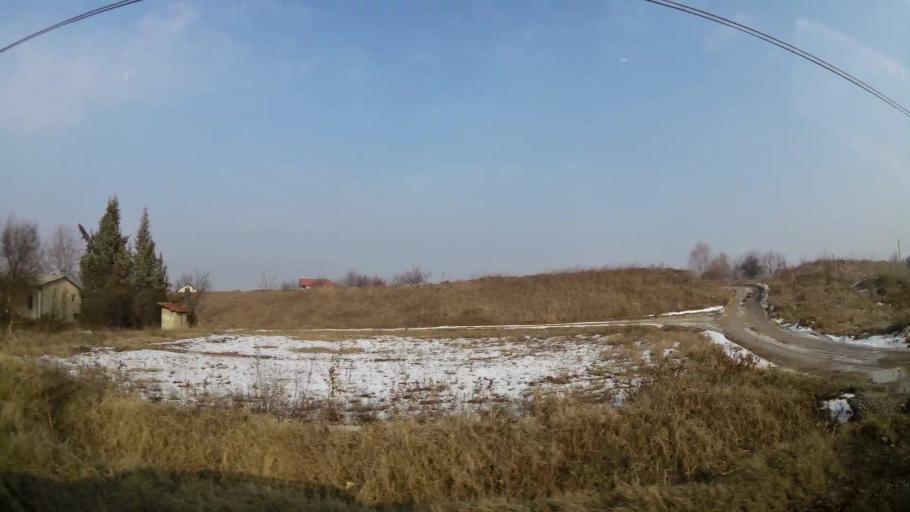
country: MK
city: Kadino
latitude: 41.9796
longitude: 21.5980
